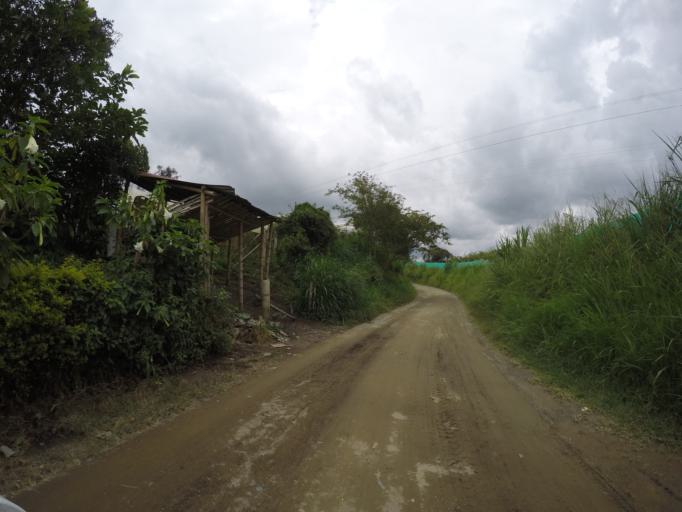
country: CO
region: Quindio
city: Circasia
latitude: 4.6214
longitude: -75.6929
